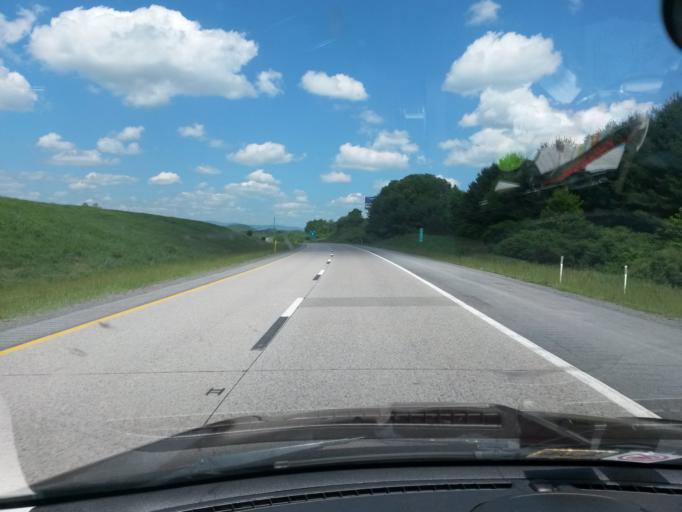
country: US
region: West Virginia
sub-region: Greenbrier County
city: Rainelle
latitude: 37.8438
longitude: -80.7320
